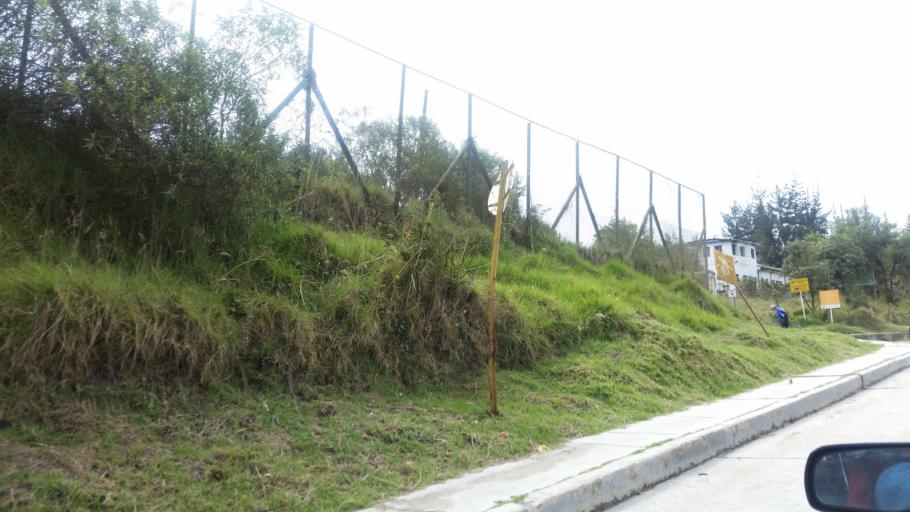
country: CO
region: Cundinamarca
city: La Calera
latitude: 4.7160
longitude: -73.9477
